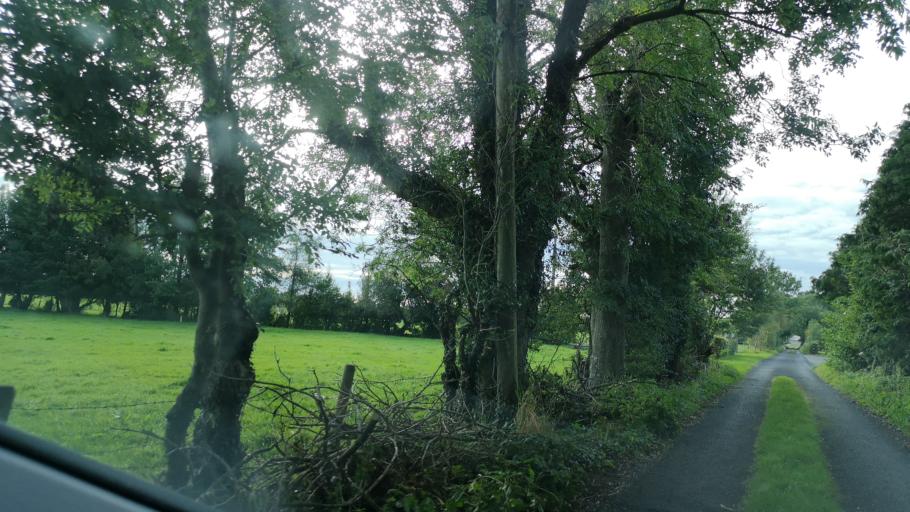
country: IE
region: Connaught
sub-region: County Galway
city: Ballinasloe
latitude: 53.3414
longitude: -8.2685
